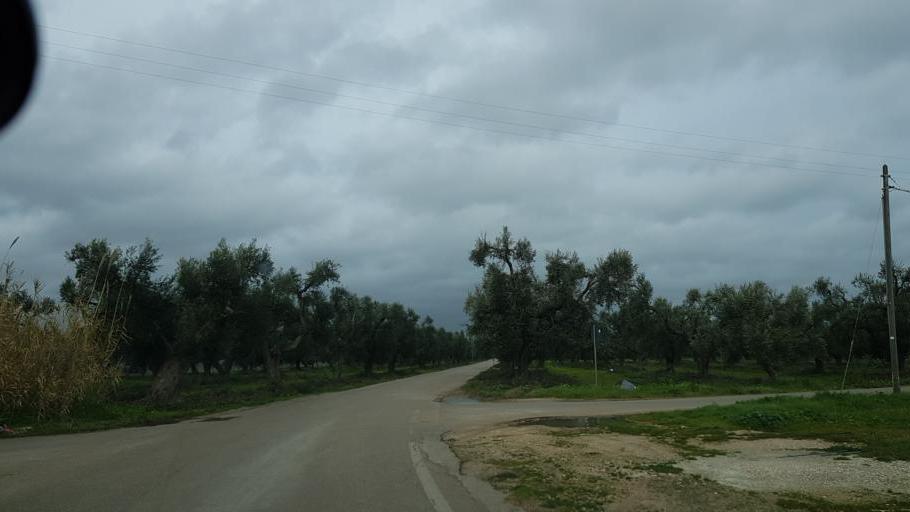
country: IT
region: Apulia
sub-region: Provincia di Brindisi
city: Brindisi
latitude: 40.5953
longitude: 17.9008
